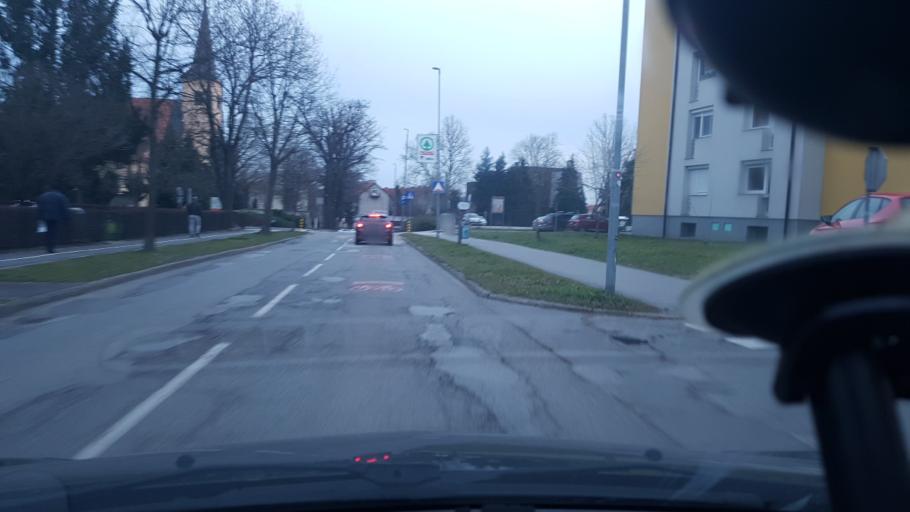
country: SI
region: Ptuj
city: Ptuj
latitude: 46.4243
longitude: 15.8734
